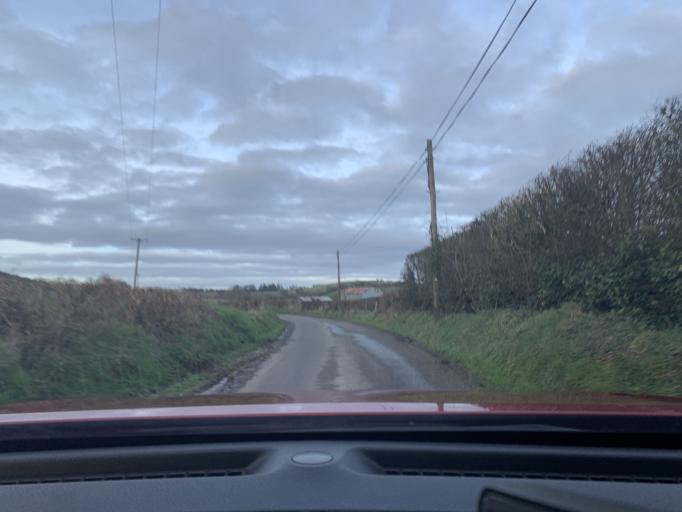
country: IE
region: Connaught
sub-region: Sligo
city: Ballymote
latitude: 54.0534
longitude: -8.5672
